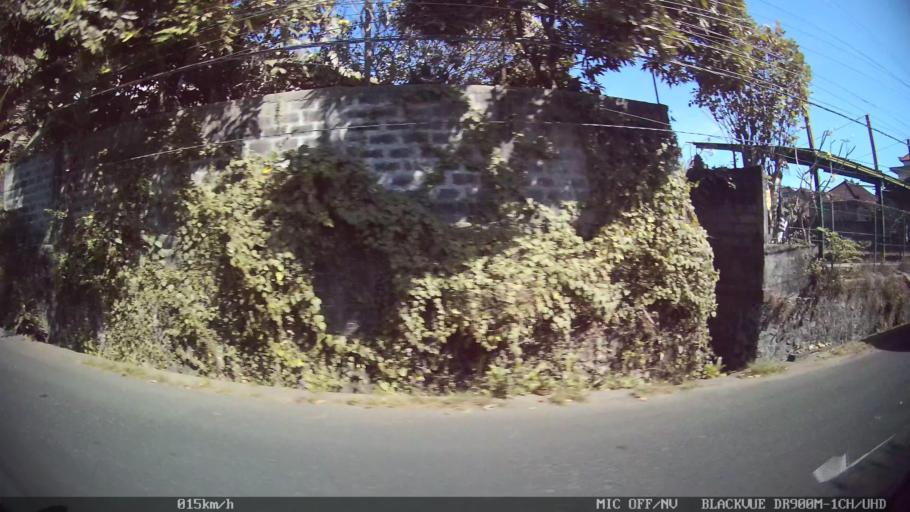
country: ID
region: Bali
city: Banjar Kertasari
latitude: -8.6312
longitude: 115.1843
